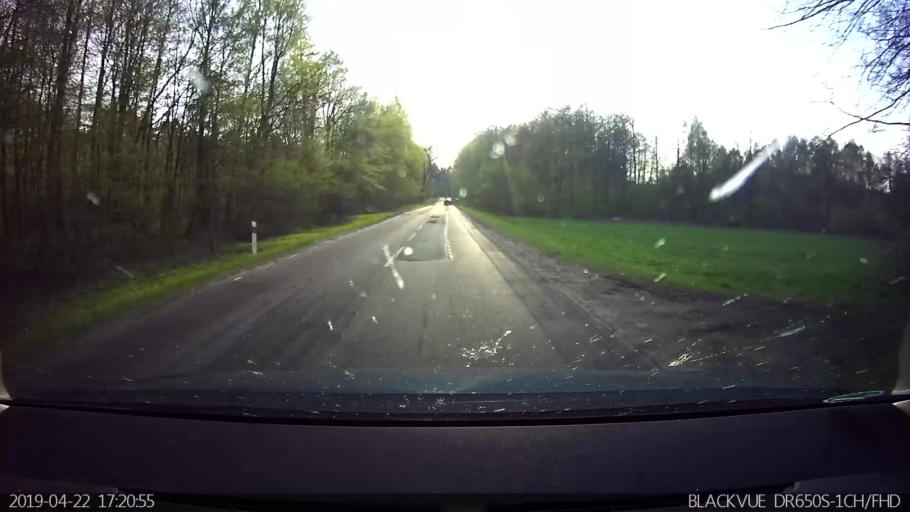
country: PL
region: Masovian Voivodeship
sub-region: Powiat sokolowski
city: Repki
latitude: 52.3880
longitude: 22.3740
